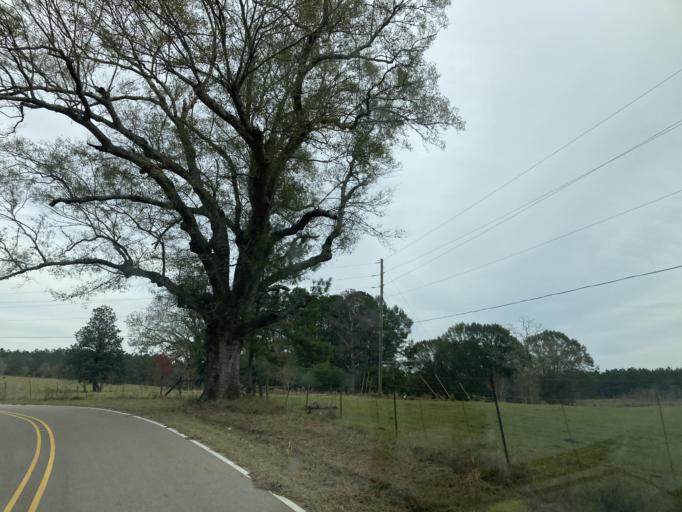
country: US
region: Mississippi
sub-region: Lamar County
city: Purvis
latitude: 31.0835
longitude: -89.4299
